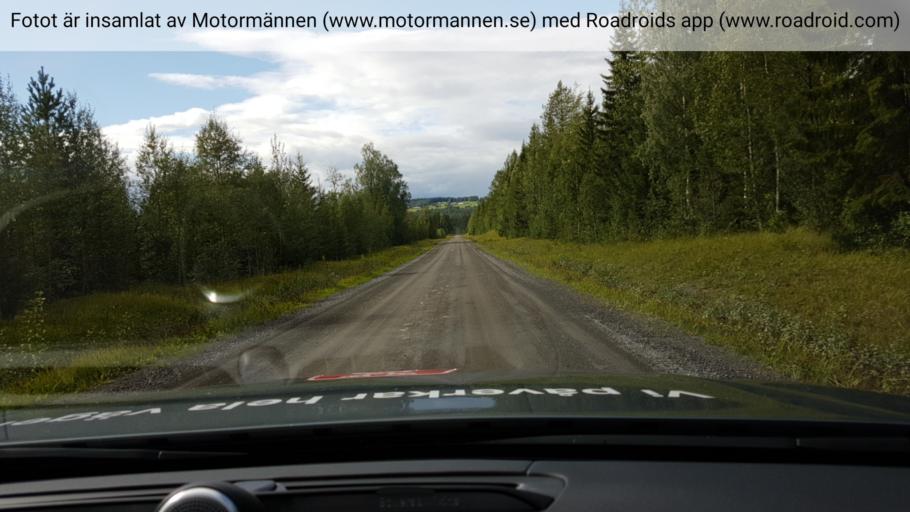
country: SE
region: Jaemtland
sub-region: OEstersunds Kommun
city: Lit
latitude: 63.6788
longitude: 14.7896
